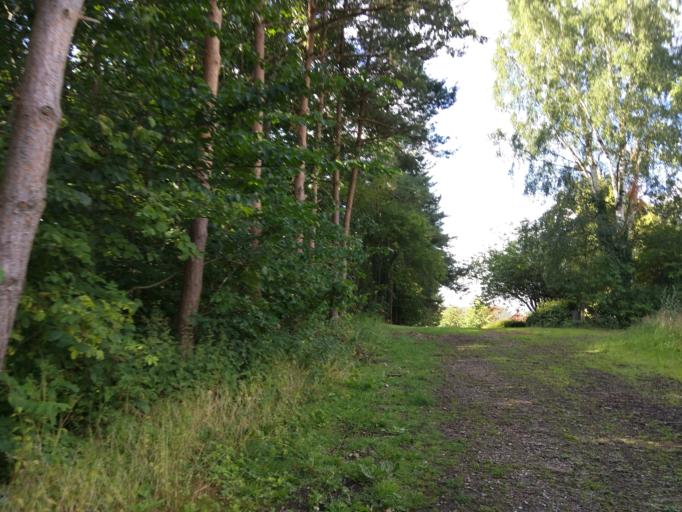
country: DK
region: Zealand
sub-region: Kalundborg Kommune
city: Svebolle
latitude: 55.6843
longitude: 11.3082
